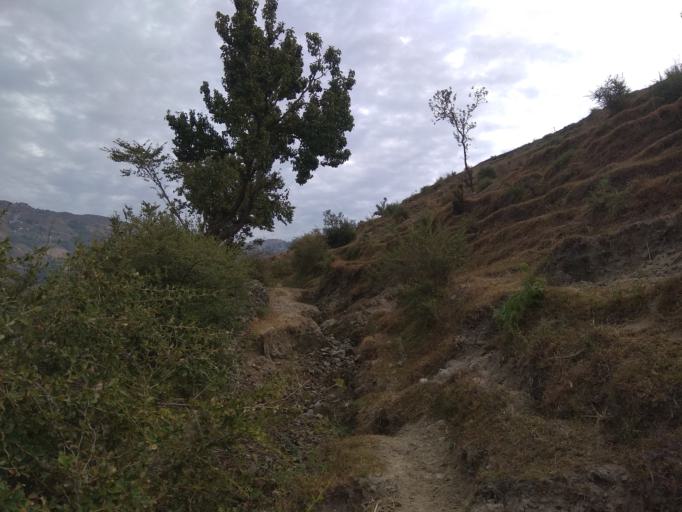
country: NP
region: Far Western
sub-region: Seti Zone
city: Achham
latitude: 29.2348
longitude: 81.6283
